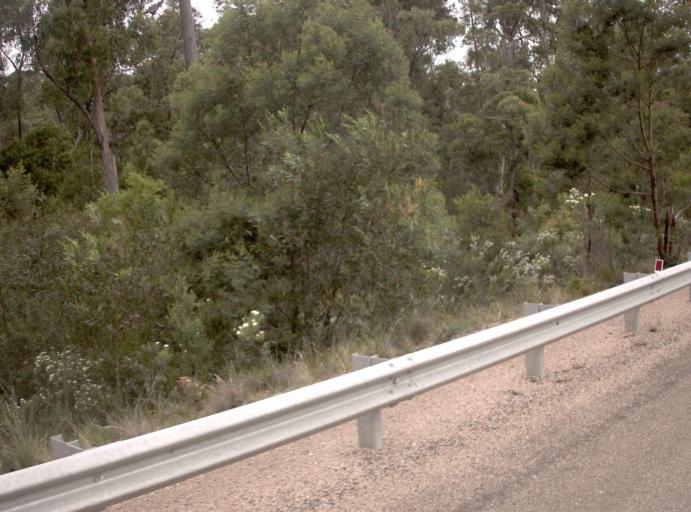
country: AU
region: Victoria
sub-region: East Gippsland
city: Lakes Entrance
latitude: -37.6980
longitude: 148.0489
